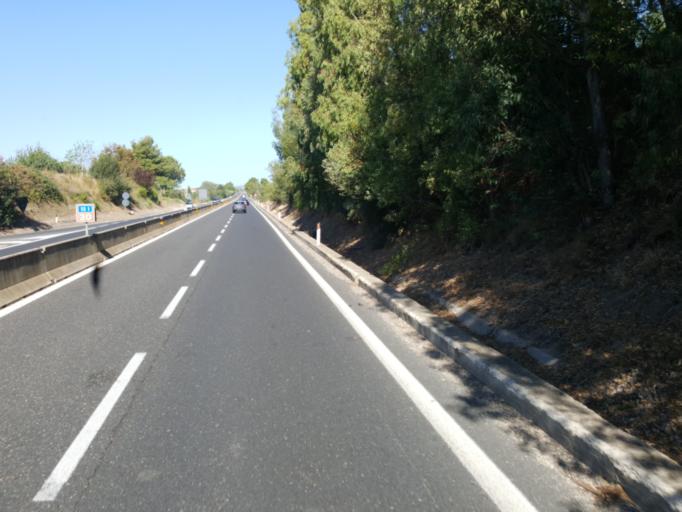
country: IT
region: Latium
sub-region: Provincia di Viterbo
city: Pescia Romana
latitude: 42.4027
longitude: 11.4985
